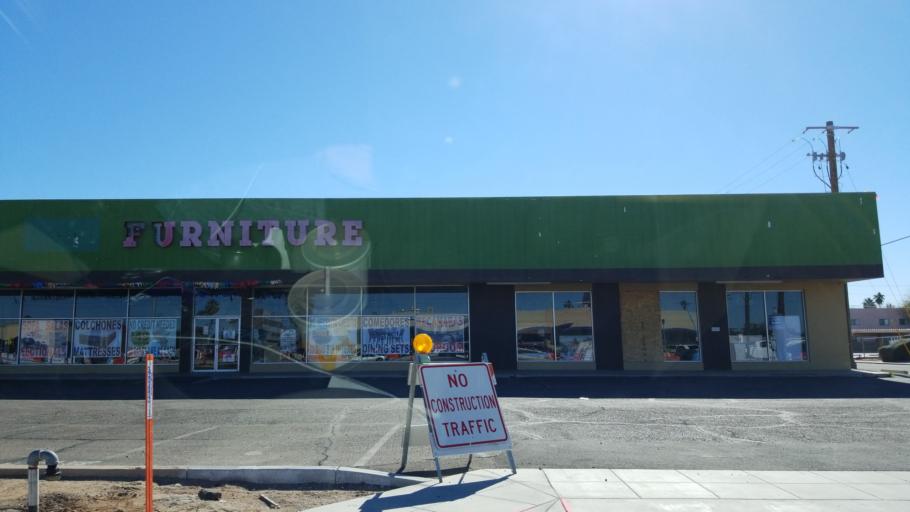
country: US
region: Arizona
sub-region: Maricopa County
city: Mesa
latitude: 33.4151
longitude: -111.8018
